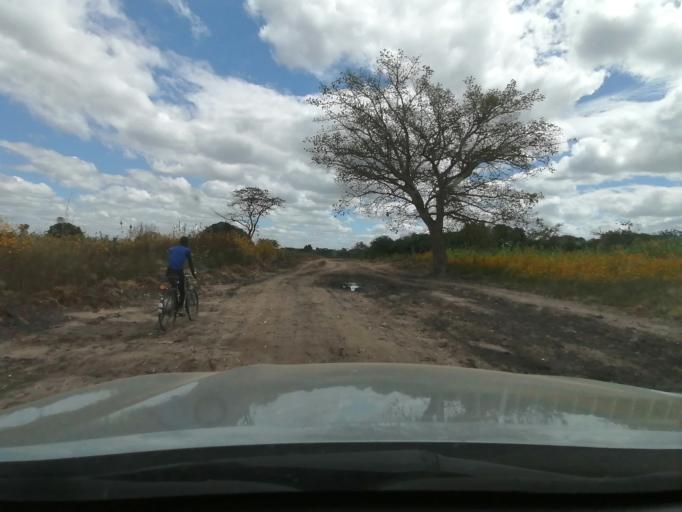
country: ZM
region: Central
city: Mumbwa
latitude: -14.5826
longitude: 27.2297
